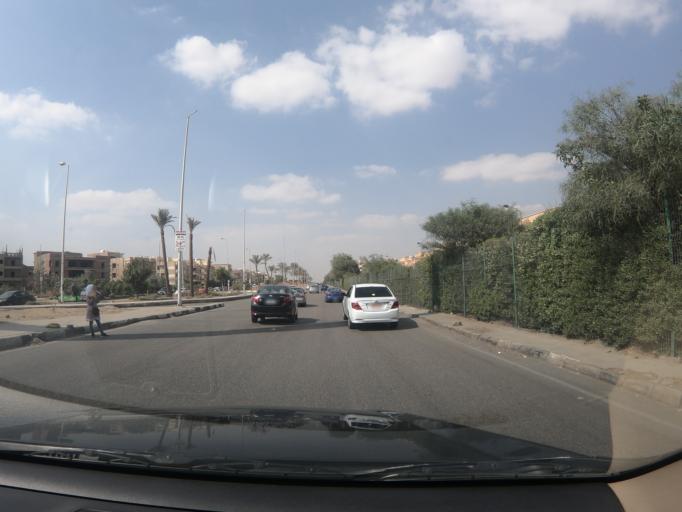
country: EG
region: Muhafazat al Qalyubiyah
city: Al Khankah
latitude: 30.0588
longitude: 31.4751
